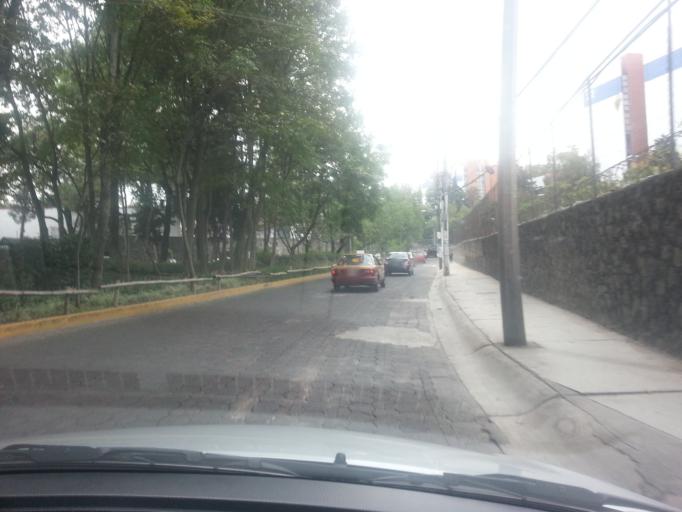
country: MX
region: Mexico City
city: Tlalpan
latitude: 19.2960
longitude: -99.1878
